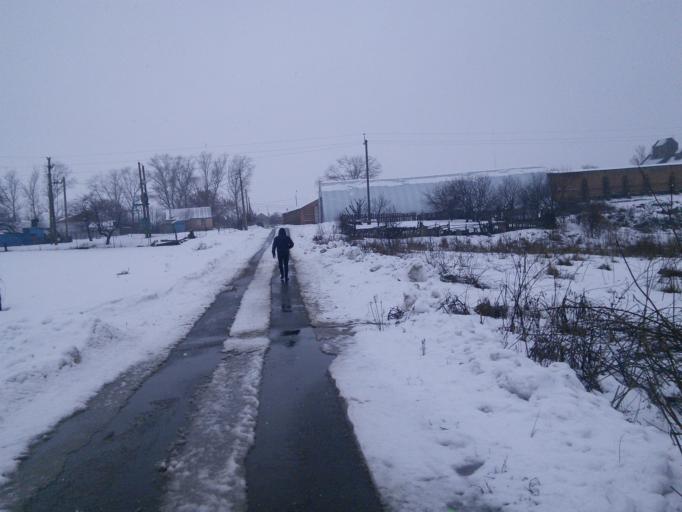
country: RU
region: Kursk
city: Chernitsyno
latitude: 51.5758
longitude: 36.0818
